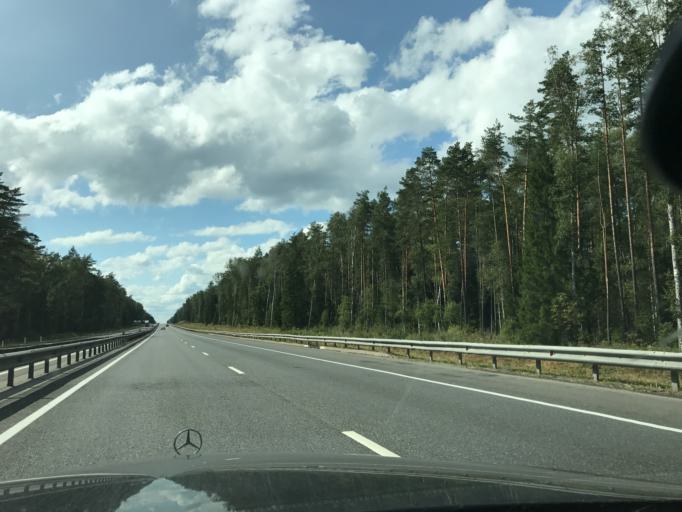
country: RU
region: Vladimir
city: Stepantsevo
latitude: 56.2230
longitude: 41.5639
